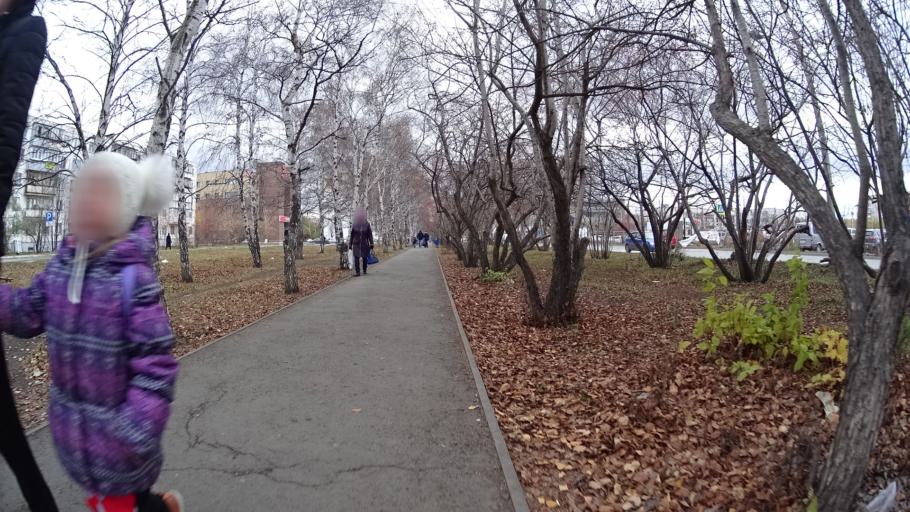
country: RU
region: Chelyabinsk
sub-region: Gorod Chelyabinsk
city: Chelyabinsk
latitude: 55.1928
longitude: 61.3217
